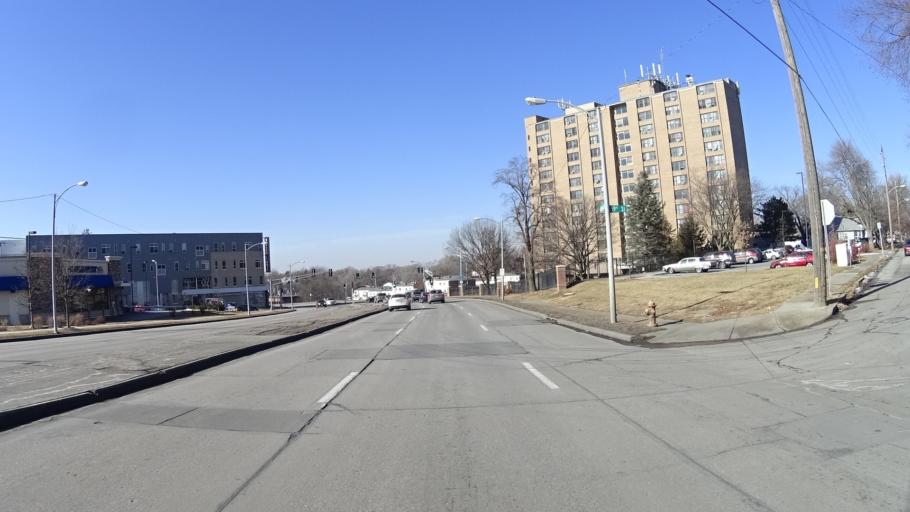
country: US
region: Nebraska
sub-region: Douglas County
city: Omaha
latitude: 41.2861
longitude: -96.0036
